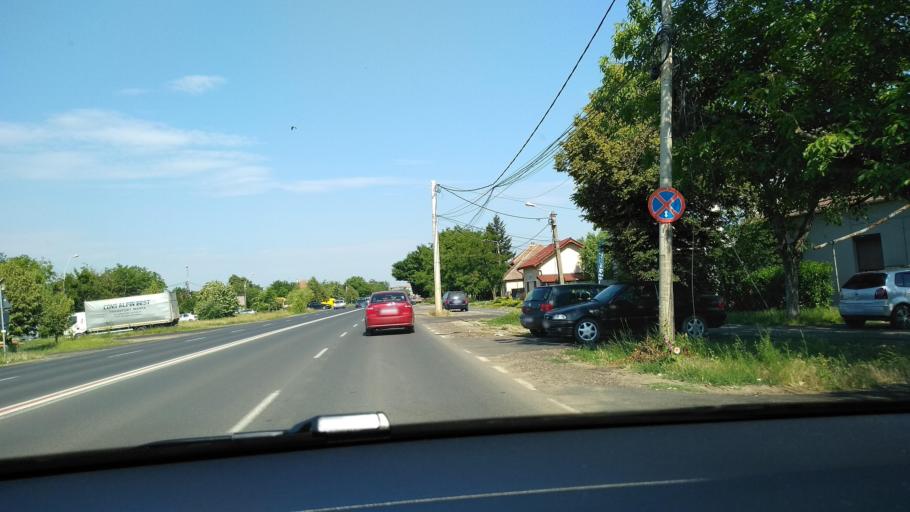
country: RO
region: Timis
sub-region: Comuna Ghiroda
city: Ghiroda
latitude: 45.7276
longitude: 21.2747
